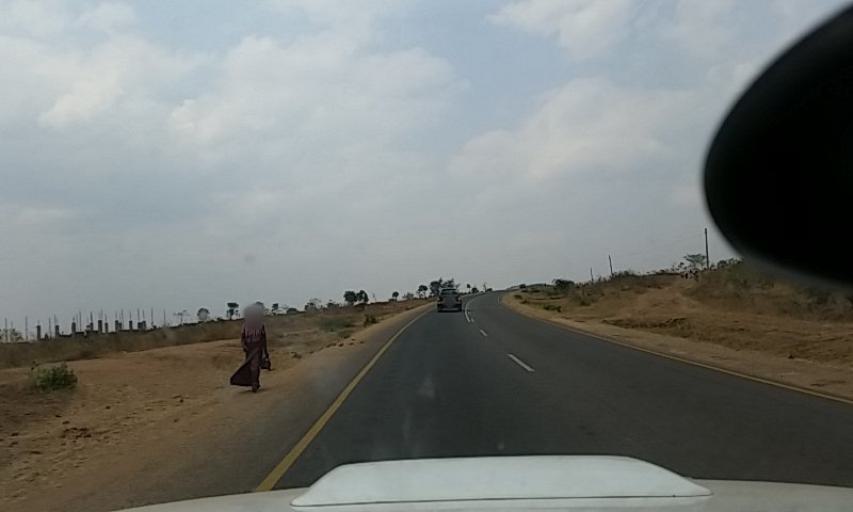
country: MW
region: Central Region
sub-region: Lilongwe District
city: Lilongwe
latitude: -13.8444
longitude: 33.8412
